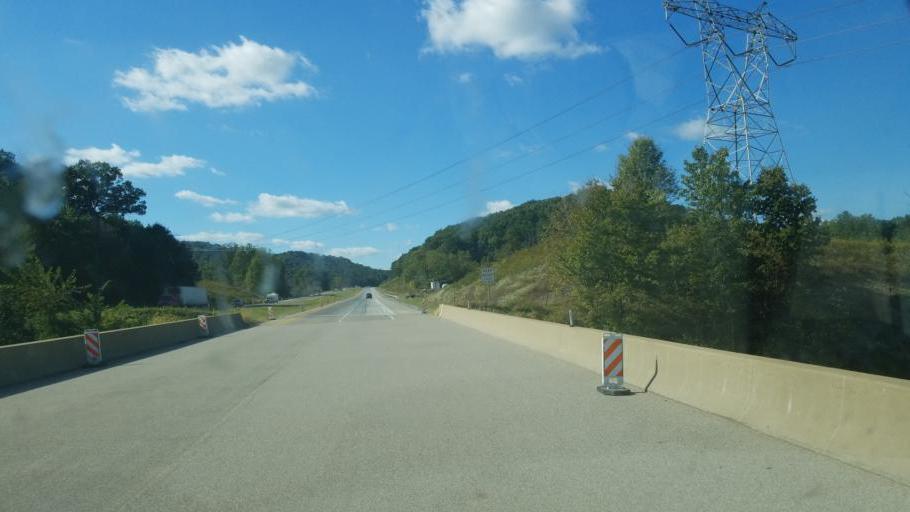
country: US
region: West Virginia
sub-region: Monongalia County
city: Star City
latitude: 39.7428
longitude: -80.0631
